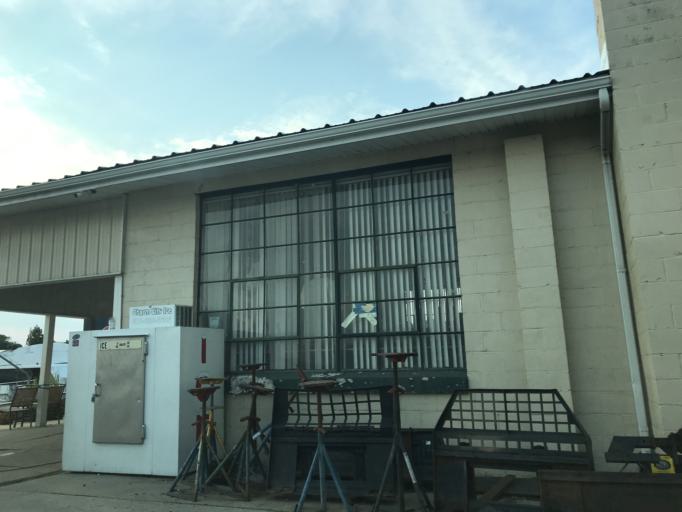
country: US
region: Maryland
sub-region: Baltimore County
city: Bowleys Quarters
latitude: 39.3317
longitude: -76.4045
